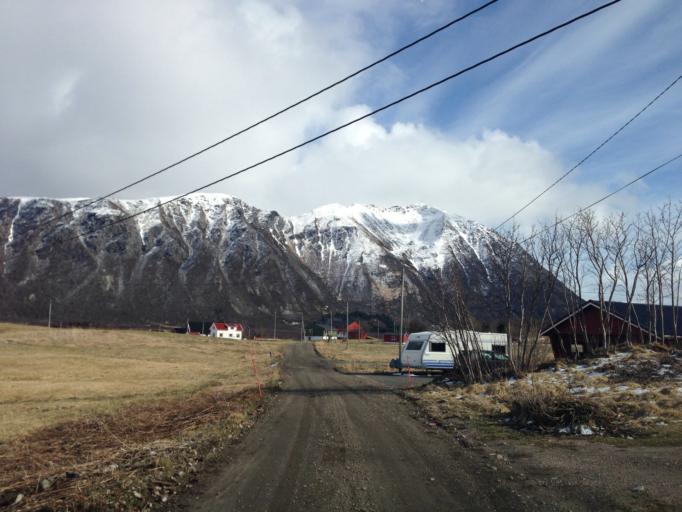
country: NO
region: Nordland
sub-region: Vagan
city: Kabelvag
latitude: 68.3906
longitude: 14.4549
